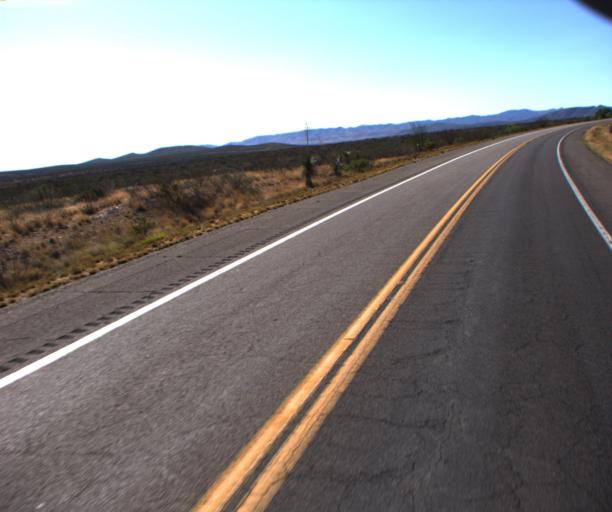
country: US
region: Arizona
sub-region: Cochise County
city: Tombstone
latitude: 31.6863
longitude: -110.0339
